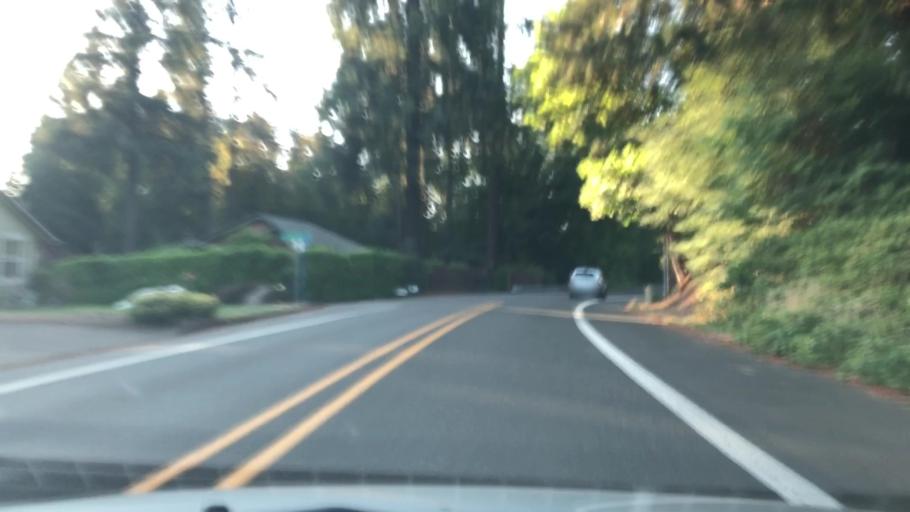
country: US
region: Oregon
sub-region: Clackamas County
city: Oak Grove
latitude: 45.4085
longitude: -122.6453
